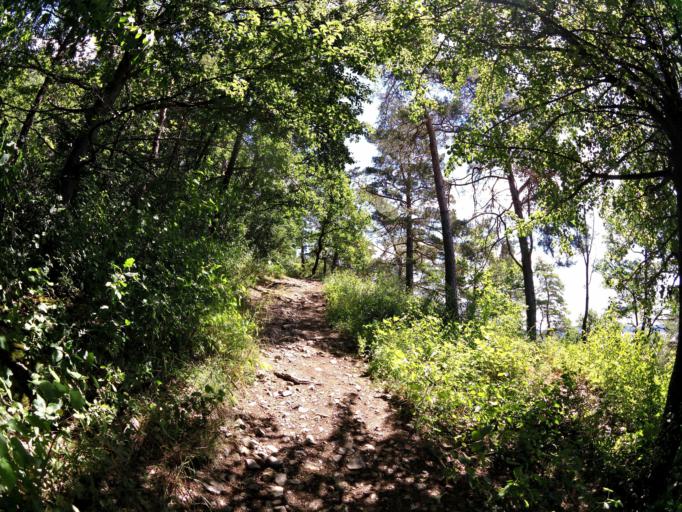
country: DE
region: Bavaria
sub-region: Regierungsbezirk Unterfranken
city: Zellingen
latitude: 49.8984
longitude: 9.8340
